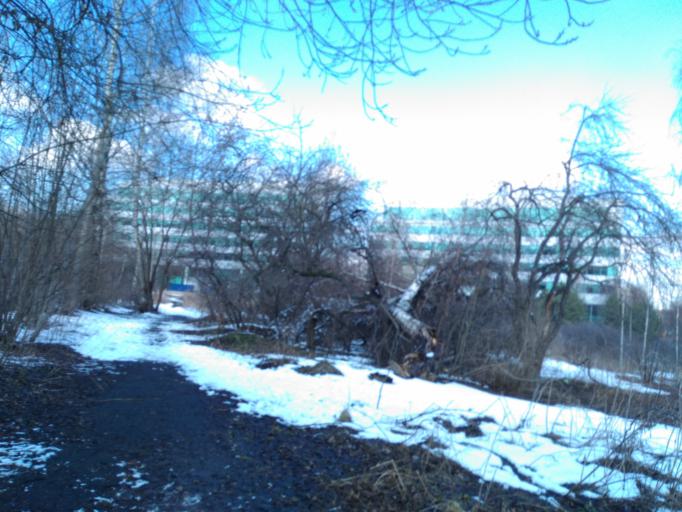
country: RU
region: Moscow
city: Shchukino
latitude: 55.7691
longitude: 37.4223
